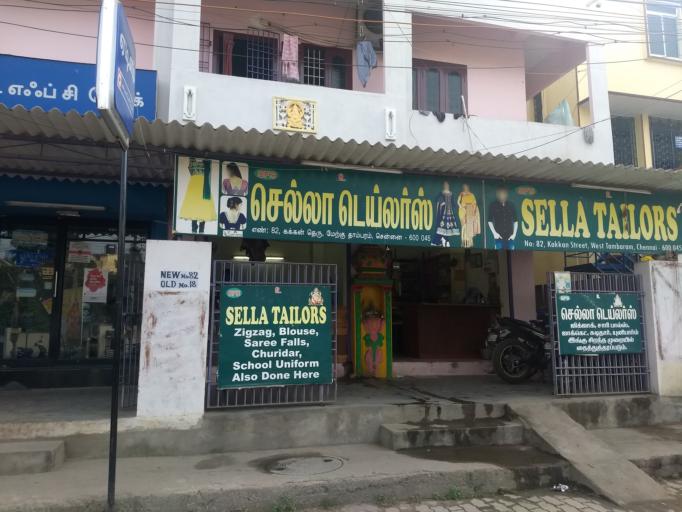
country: IN
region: Tamil Nadu
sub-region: Kancheepuram
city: Vandalur
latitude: 12.9285
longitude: 80.1121
